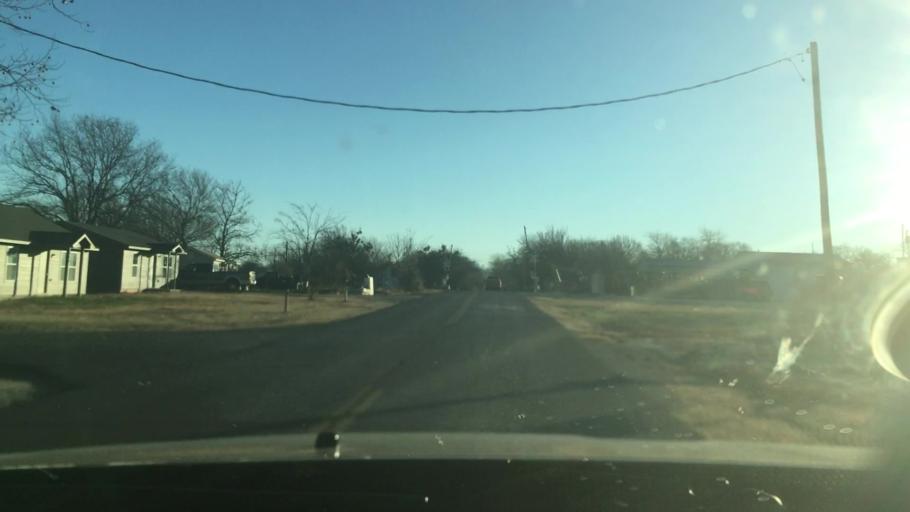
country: US
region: Oklahoma
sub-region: Pontotoc County
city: Ada
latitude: 34.7713
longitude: -96.6900
